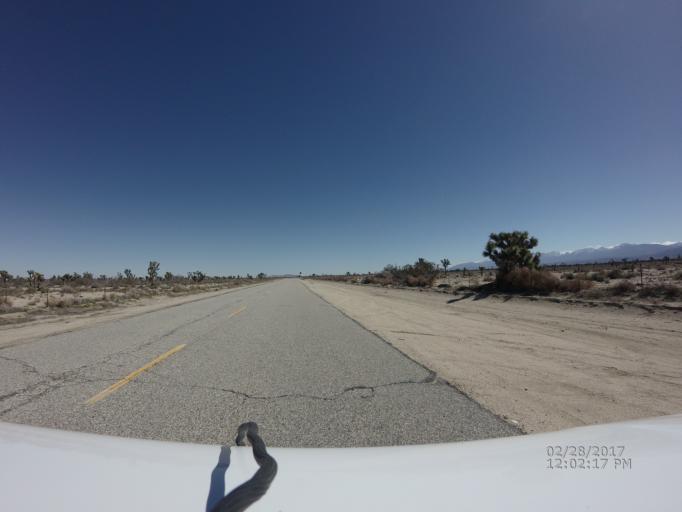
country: US
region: California
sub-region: Los Angeles County
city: Palmdale
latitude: 34.5947
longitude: -118.0453
